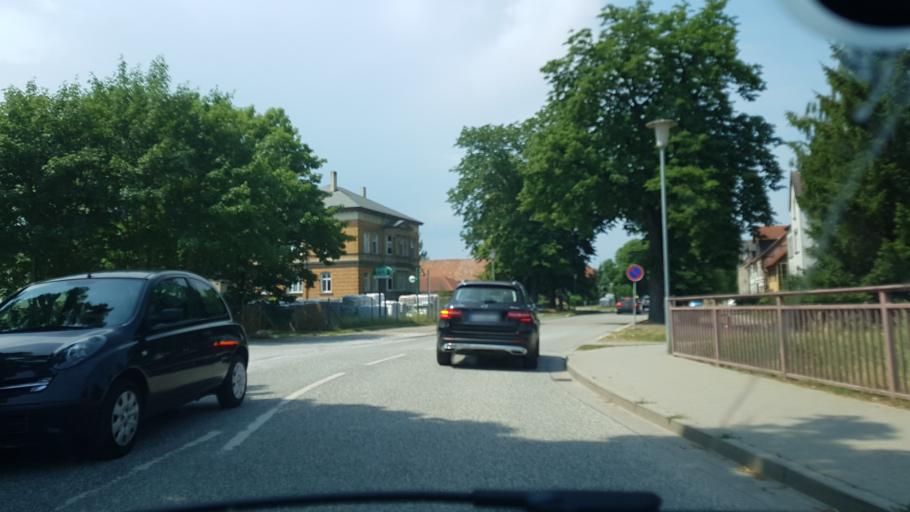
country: DE
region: Saxony-Anhalt
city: Osterwieck
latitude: 51.9671
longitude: 10.7201
